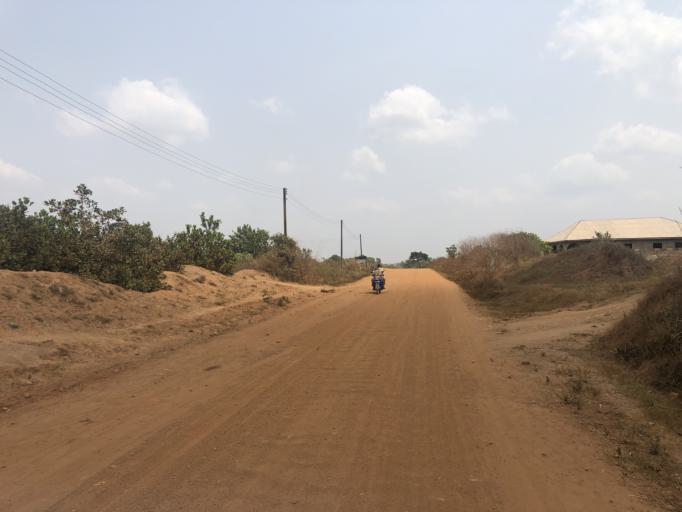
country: NG
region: Osun
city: Bode Osi
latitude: 7.8023
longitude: 4.1522
